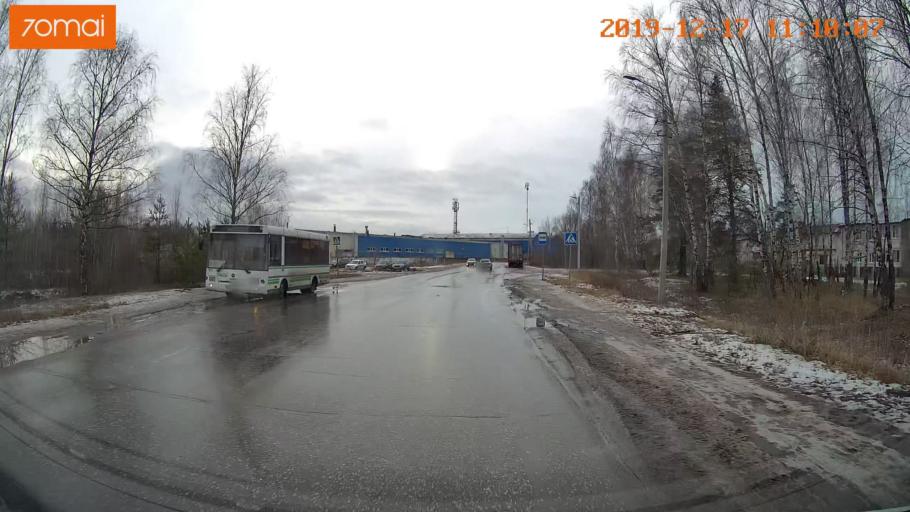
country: RU
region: Vladimir
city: Gus'-Khrustal'nyy
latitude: 55.5953
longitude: 40.6420
